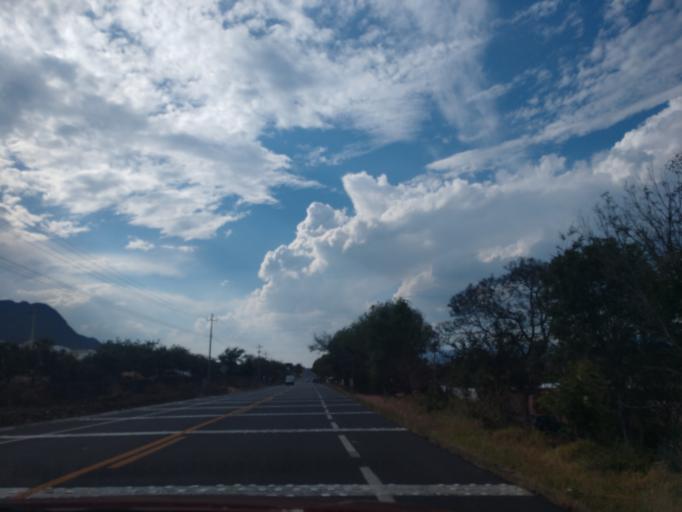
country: MX
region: Jalisco
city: Chapala
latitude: 20.1699
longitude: -103.2140
